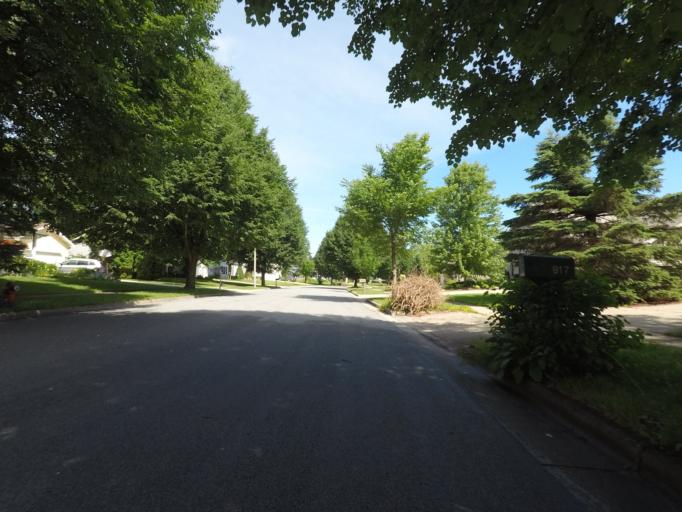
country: US
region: Wisconsin
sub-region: Dane County
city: Middleton
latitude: 43.0810
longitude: -89.5159
